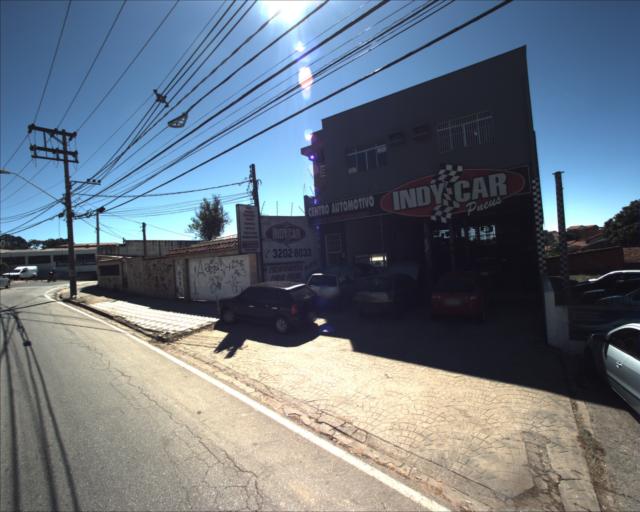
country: BR
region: Sao Paulo
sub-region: Sorocaba
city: Sorocaba
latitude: -23.5012
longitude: -47.4817
